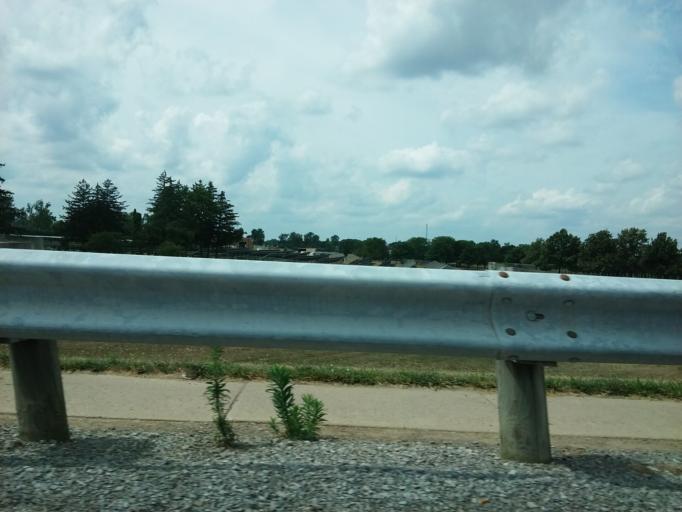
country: US
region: Ohio
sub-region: Hancock County
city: Findlay
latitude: 41.0483
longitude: -83.6647
